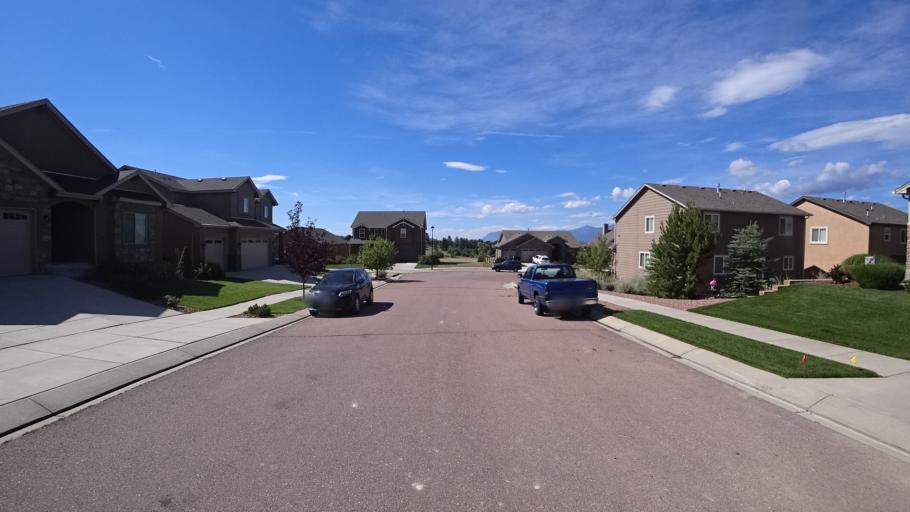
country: US
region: Colorado
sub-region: El Paso County
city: Gleneagle
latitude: 39.0240
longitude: -104.8086
